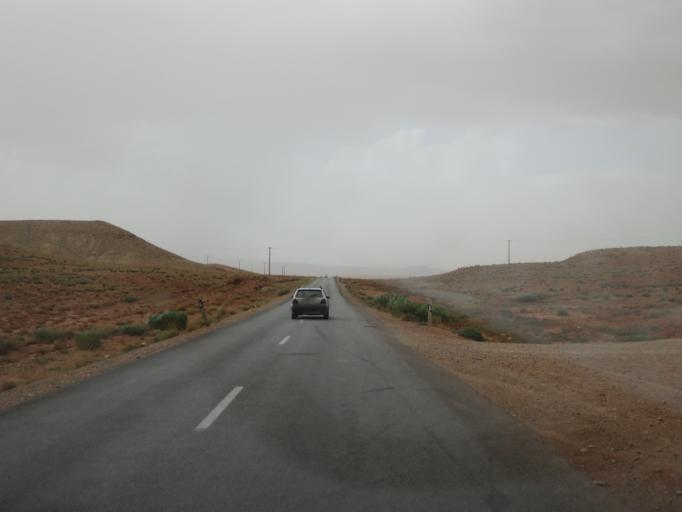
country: MA
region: Meknes-Tafilalet
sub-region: Khenifra
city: Itzer
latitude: 32.8625
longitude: -4.9451
